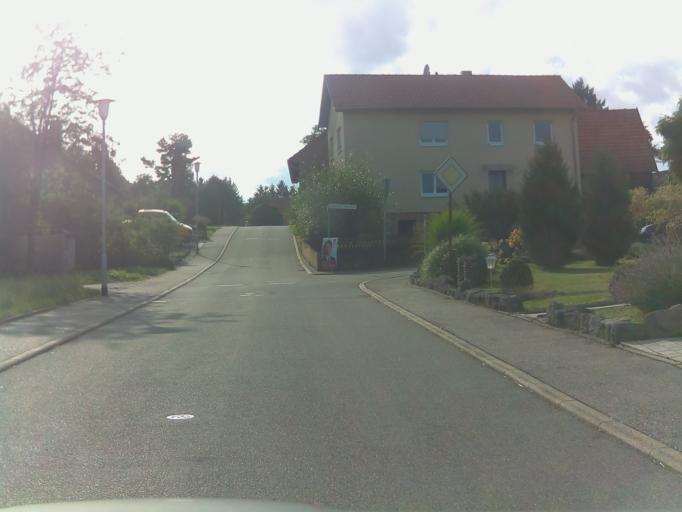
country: DE
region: Hesse
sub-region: Regierungsbezirk Darmstadt
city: Hesseneck
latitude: 49.5744
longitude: 9.0856
